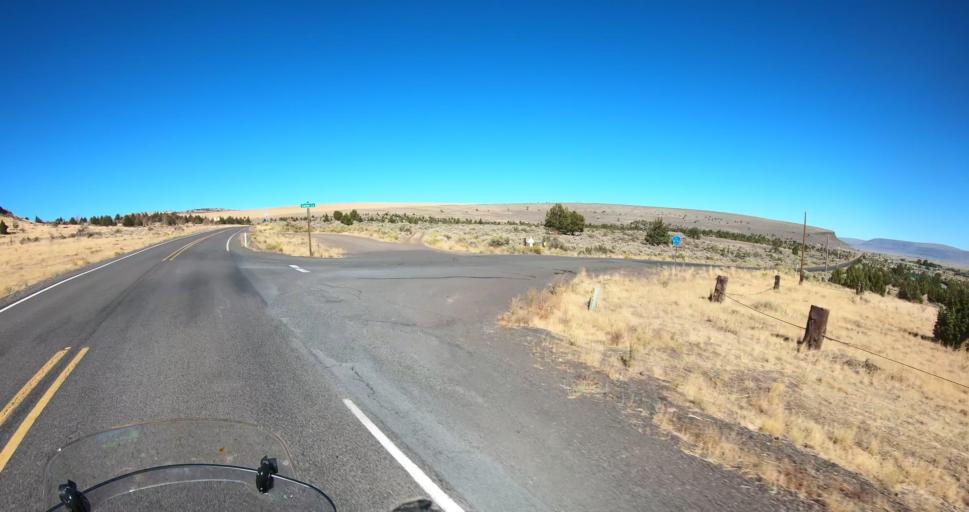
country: US
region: Oregon
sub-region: Lake County
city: Lakeview
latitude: 43.0054
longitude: -120.7759
